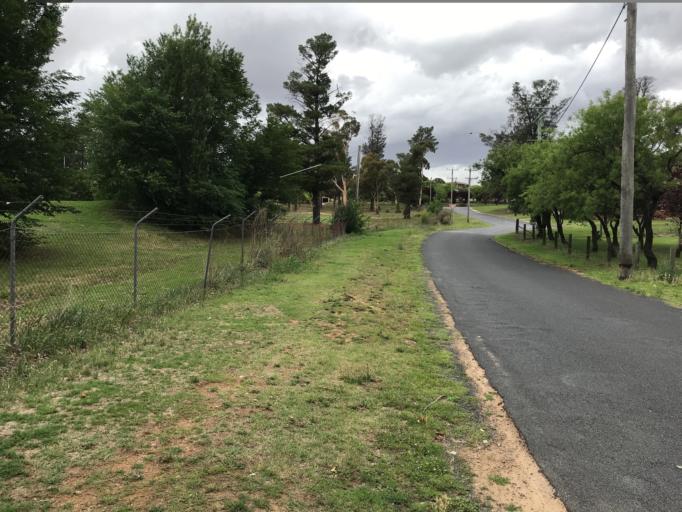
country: AU
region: New South Wales
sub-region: Cooma-Monaro
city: Cooma
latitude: -36.2410
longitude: 149.1216
